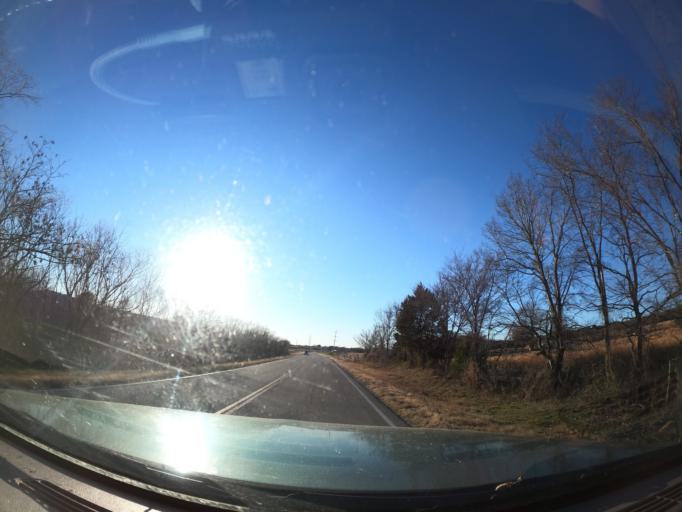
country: US
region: Oklahoma
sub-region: Pittsburg County
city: Hartshorne
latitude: 34.8870
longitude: -95.4833
